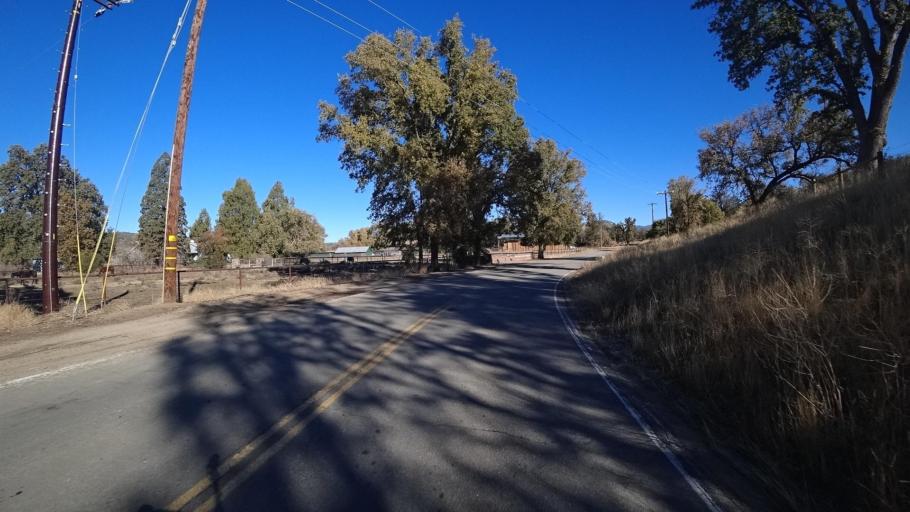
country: US
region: California
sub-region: Kern County
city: Alta Sierra
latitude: 35.7700
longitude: -118.7104
